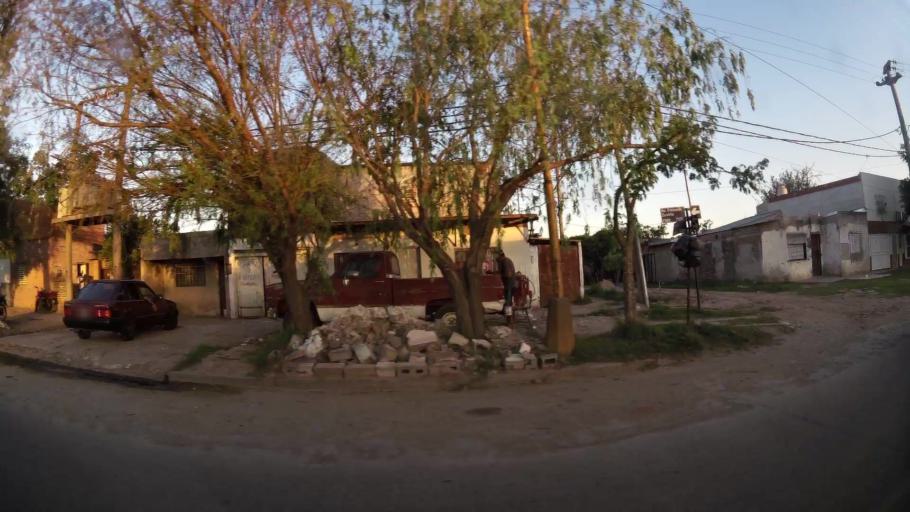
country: AR
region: Santa Fe
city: Santa Fe de la Vera Cruz
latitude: -31.5944
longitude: -60.6996
